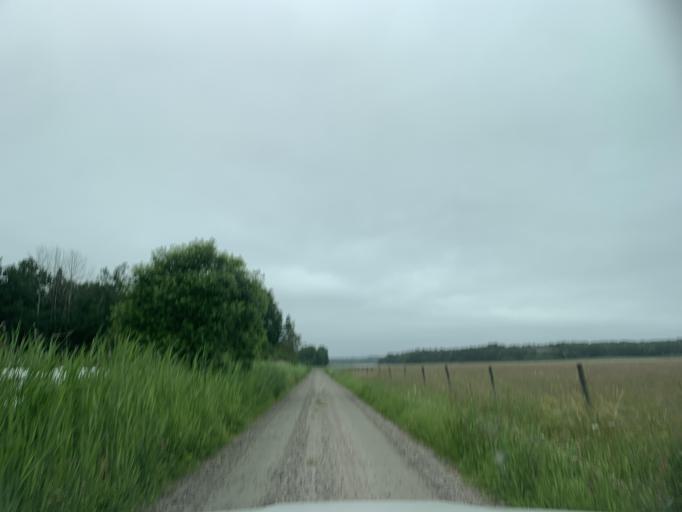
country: SE
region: Vaestra Goetaland
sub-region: Stromstads Kommun
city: Stroemstad
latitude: 58.8627
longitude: 11.2180
